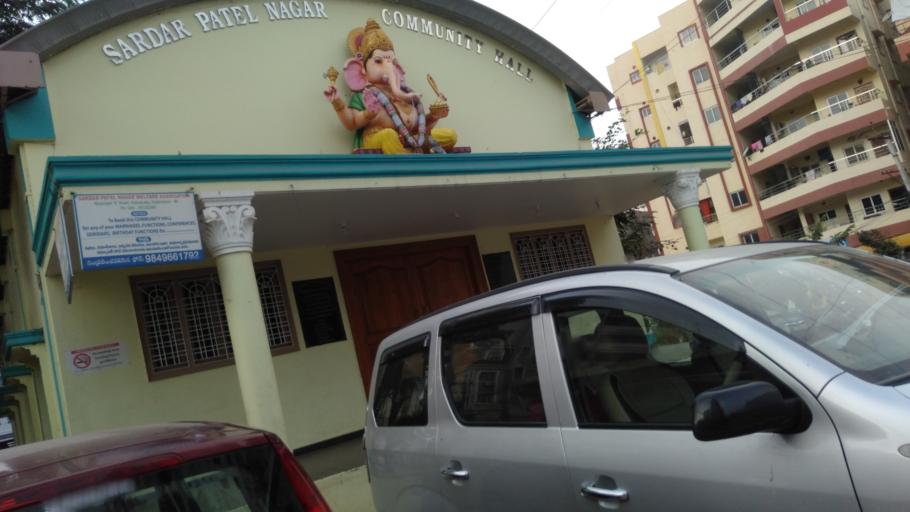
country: IN
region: Telangana
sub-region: Rangareddi
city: Kukatpalli
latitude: 17.4970
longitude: 78.3889
